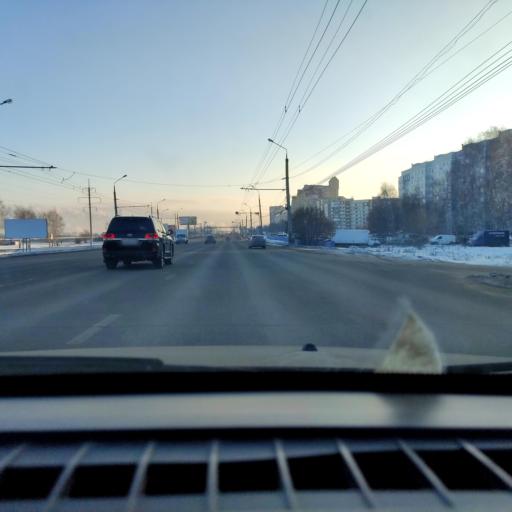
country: RU
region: Samara
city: Tol'yatti
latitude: 53.5487
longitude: 49.3526
